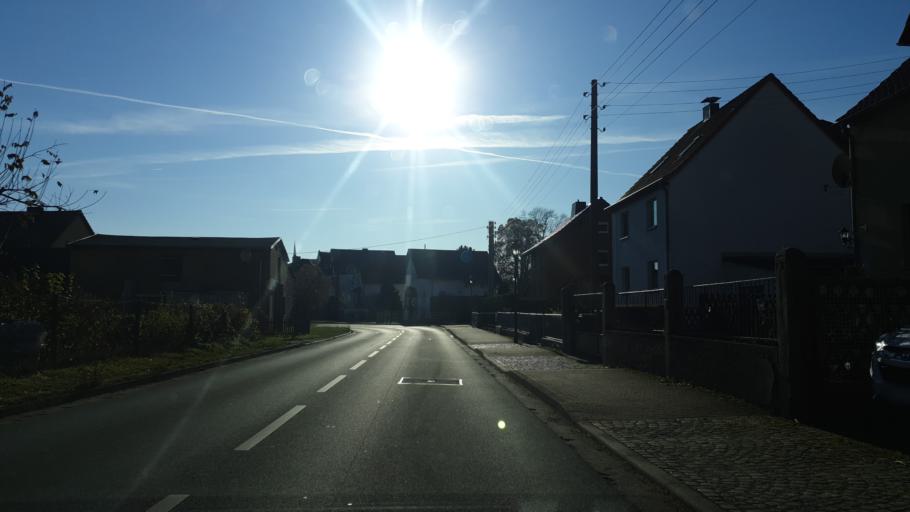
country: DE
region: Thuringia
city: Hartmannsdorf
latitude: 50.9789
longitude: 11.9786
